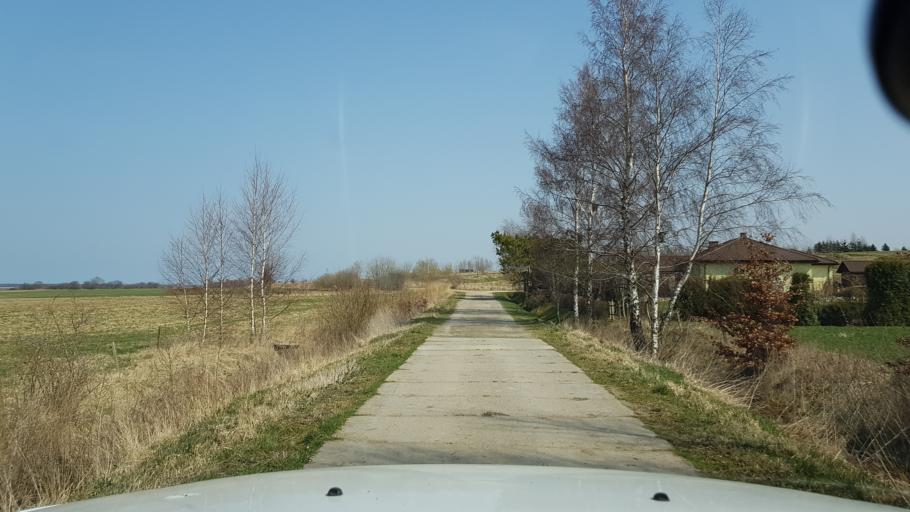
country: PL
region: West Pomeranian Voivodeship
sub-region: Powiat slawienski
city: Darlowo
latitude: 54.4607
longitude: 16.4363
